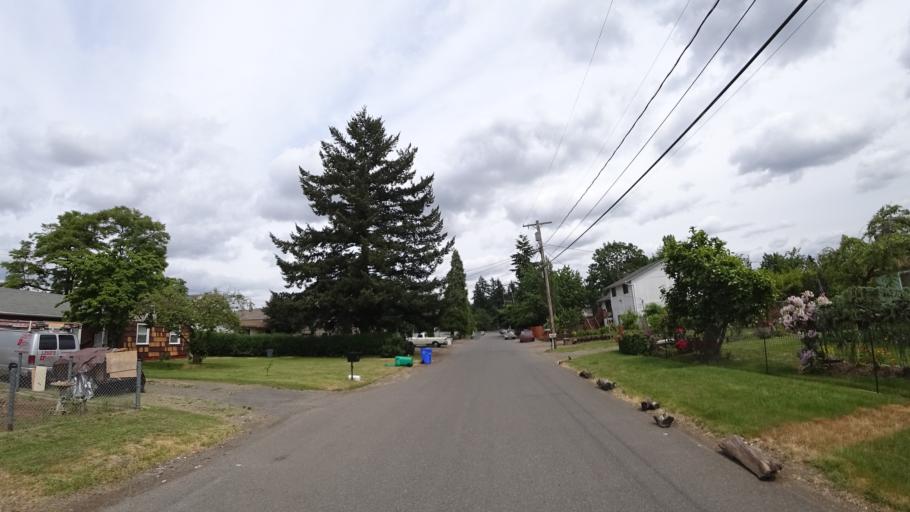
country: US
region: Oregon
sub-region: Multnomah County
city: Lents
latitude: 45.4884
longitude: -122.5401
